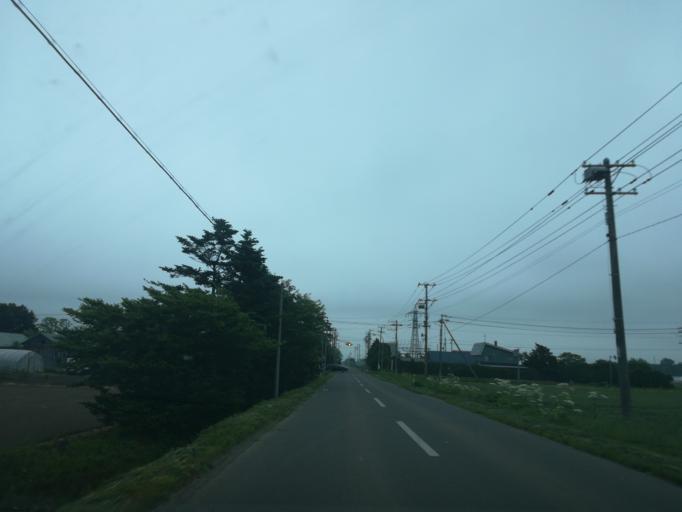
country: JP
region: Hokkaido
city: Ebetsu
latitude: 43.0604
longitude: 141.6230
